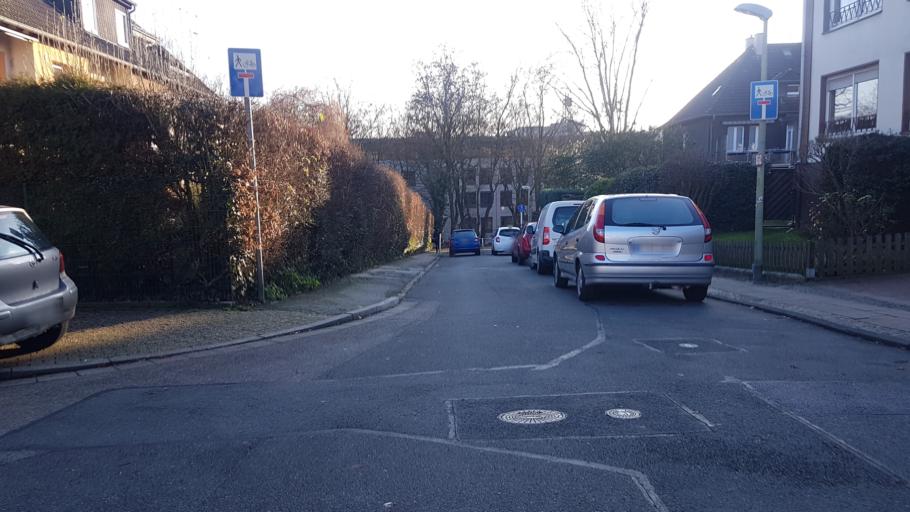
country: DE
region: North Rhine-Westphalia
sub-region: Regierungsbezirk Dusseldorf
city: Essen
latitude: 51.4297
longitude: 7.0420
